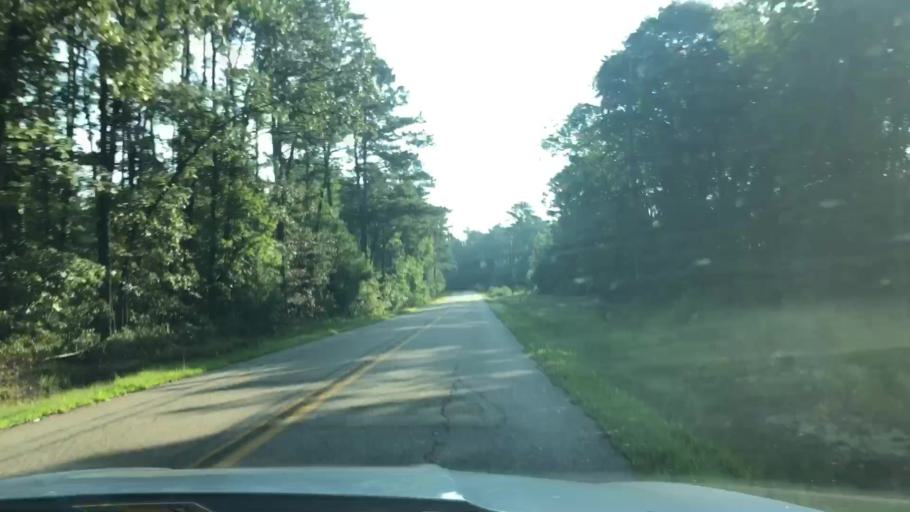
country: US
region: Virginia
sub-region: King William County
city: West Point
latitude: 37.6099
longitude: -76.7155
